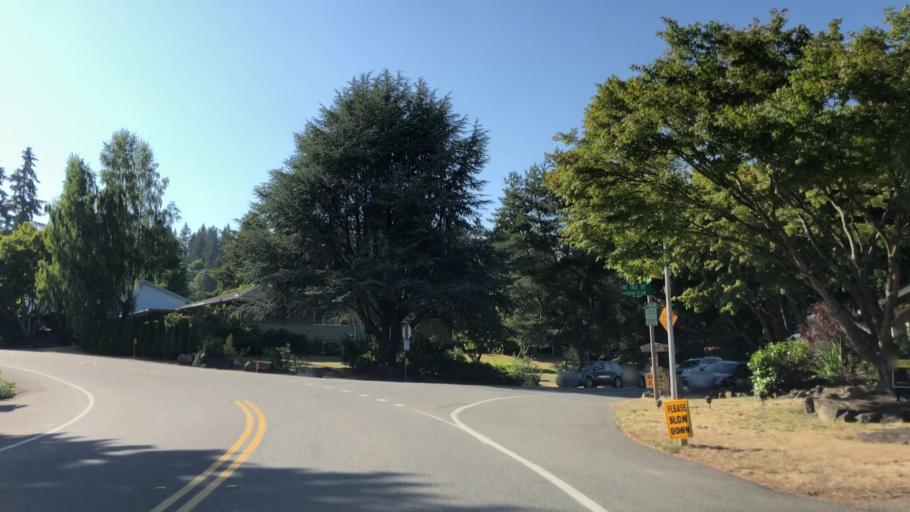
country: US
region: Washington
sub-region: King County
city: Lake Forest Park
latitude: 47.7606
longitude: -122.2656
